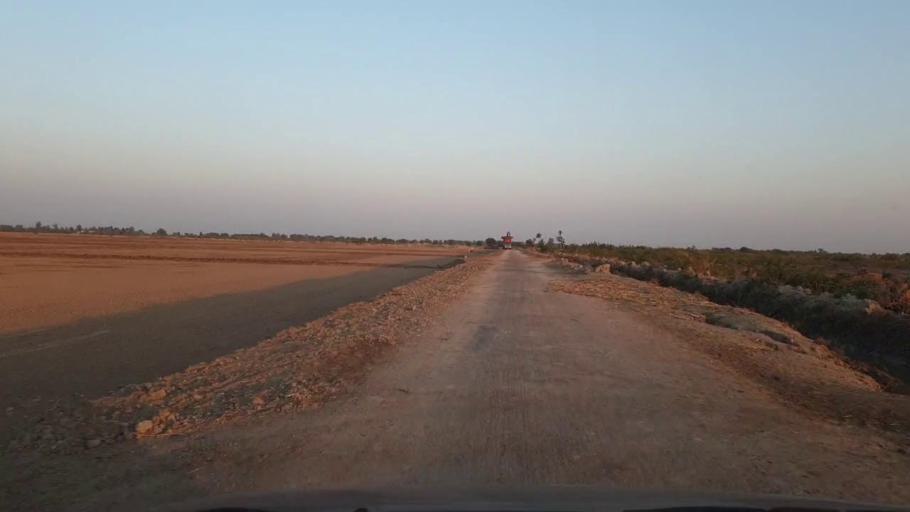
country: PK
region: Sindh
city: Digri
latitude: 25.1380
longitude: 69.2489
